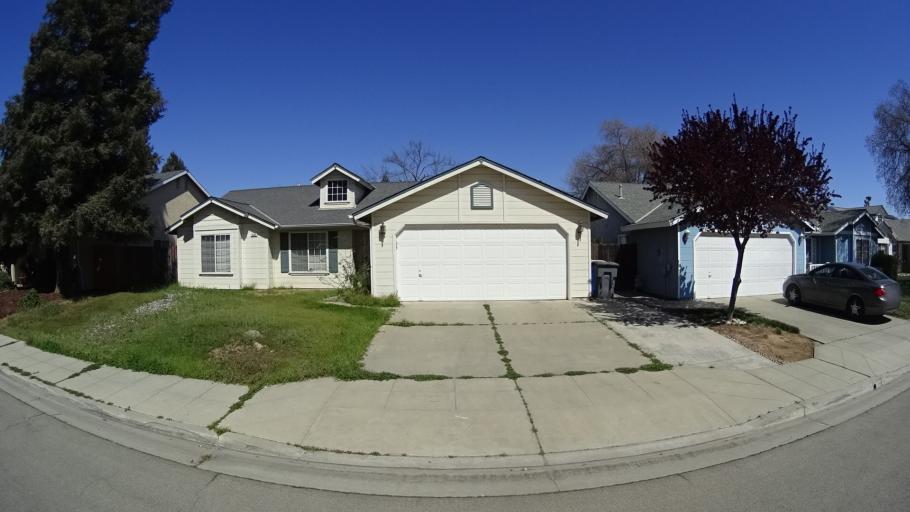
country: US
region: California
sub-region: Fresno County
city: West Park
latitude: 36.7837
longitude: -119.8872
